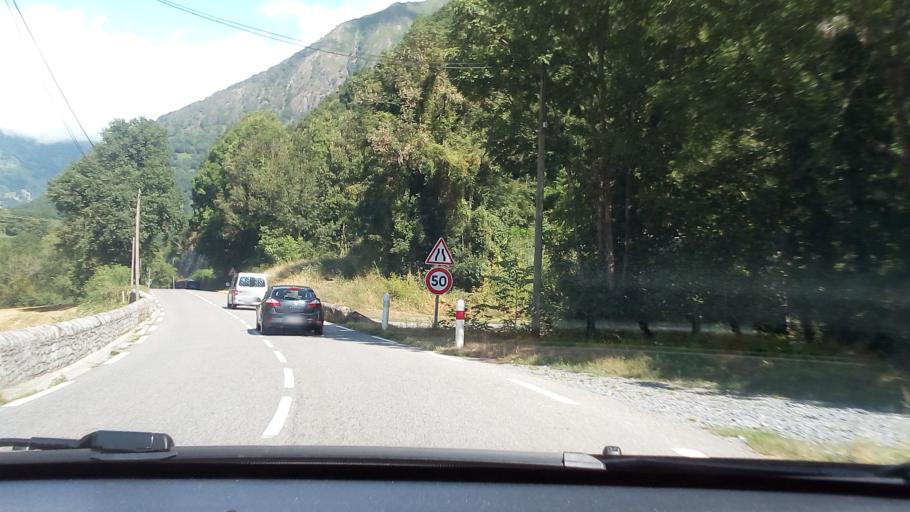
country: FR
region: Aquitaine
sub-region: Departement des Pyrenees-Atlantiques
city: Laruns
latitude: 42.9297
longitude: -0.5813
